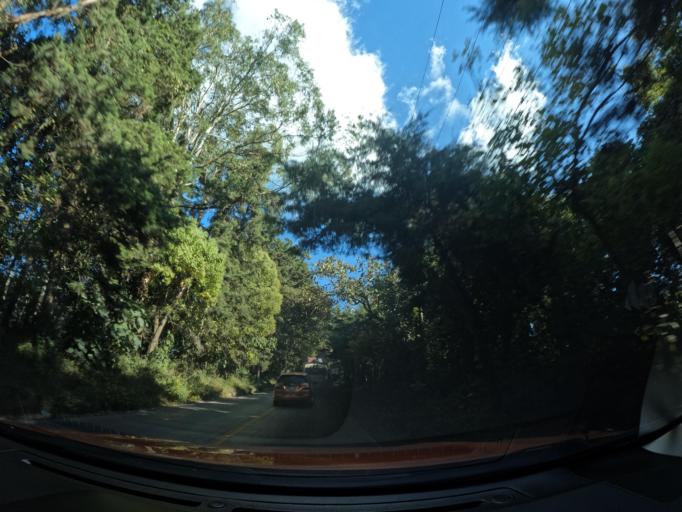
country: GT
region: Sacatepequez
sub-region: Municipio de Santa Maria de Jesus
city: Santa Maria de Jesus
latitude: 14.5088
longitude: -90.7183
